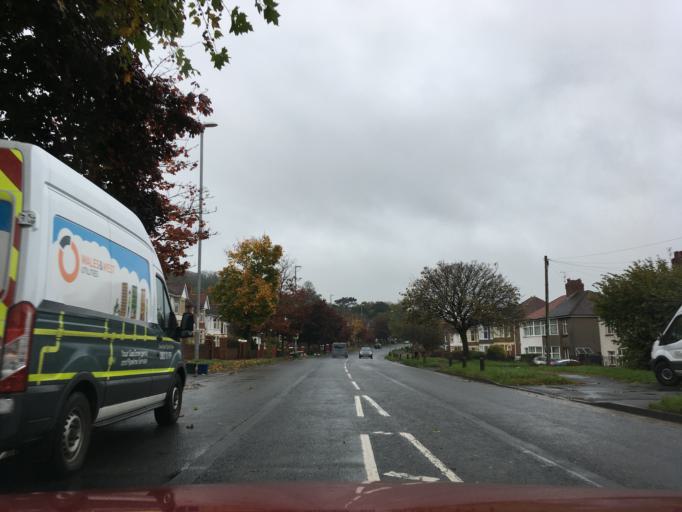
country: GB
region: Wales
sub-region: Newport
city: Caerleon
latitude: 51.5979
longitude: -2.9358
